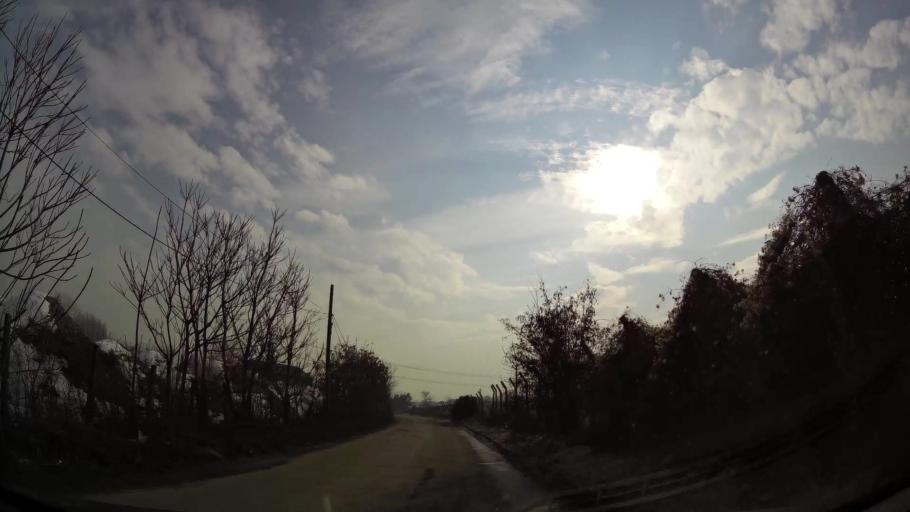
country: MK
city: Krushopek
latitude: 42.0156
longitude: 21.3691
